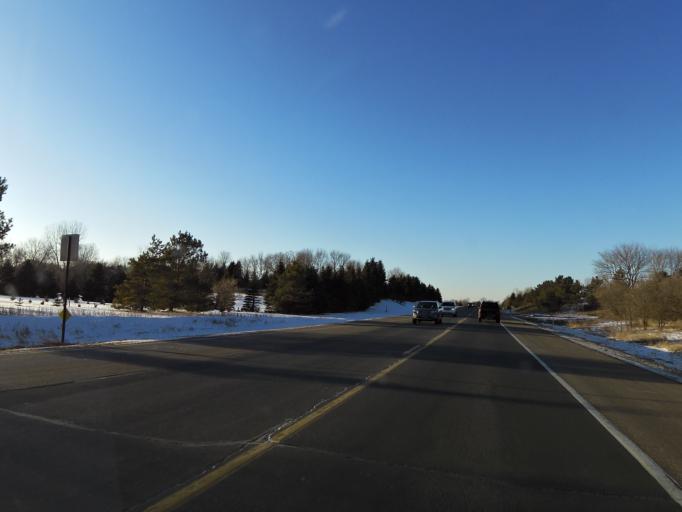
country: US
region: Minnesota
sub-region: Washington County
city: Lake Elmo
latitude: 44.9770
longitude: -92.8578
